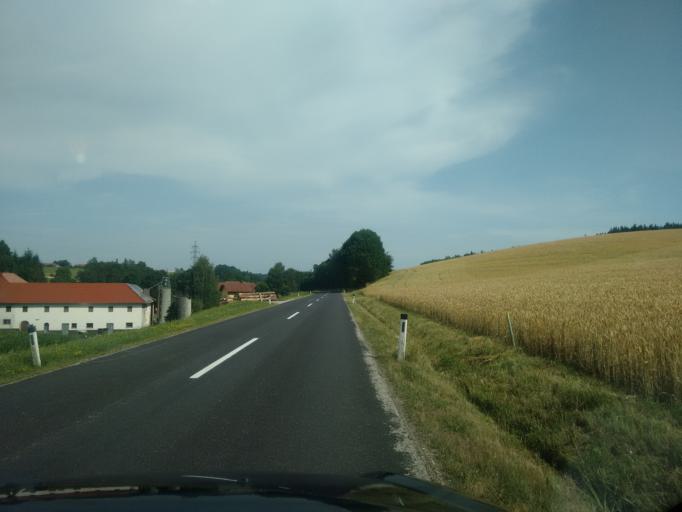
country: AT
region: Upper Austria
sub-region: Wels-Land
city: Offenhausen
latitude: 48.1888
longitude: 13.8448
